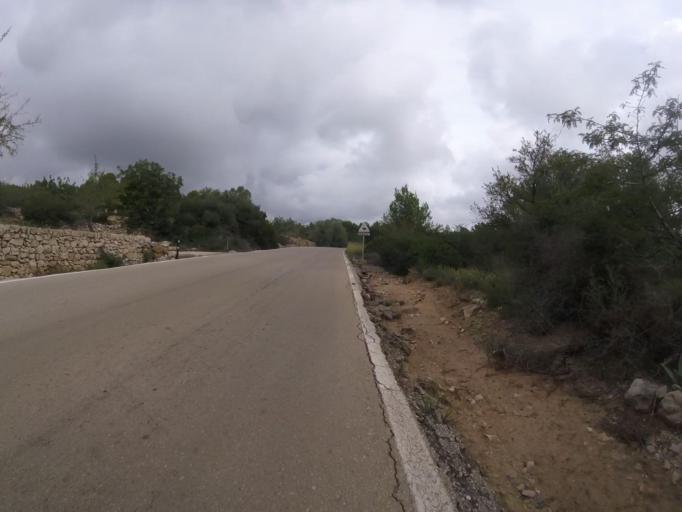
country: ES
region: Valencia
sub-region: Provincia de Castello
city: Cabanes
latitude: 40.1570
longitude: 0.0833
